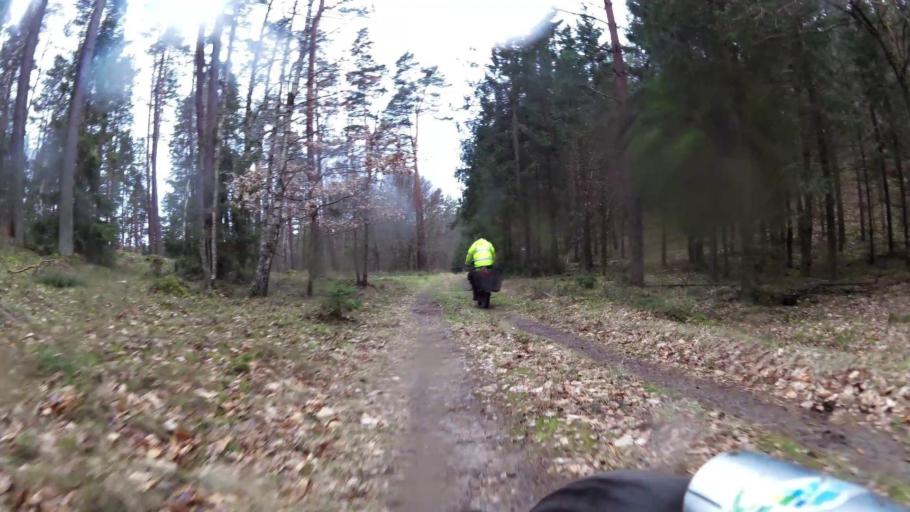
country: PL
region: Pomeranian Voivodeship
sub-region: Powiat bytowski
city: Trzebielino
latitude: 54.0774
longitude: 17.1113
